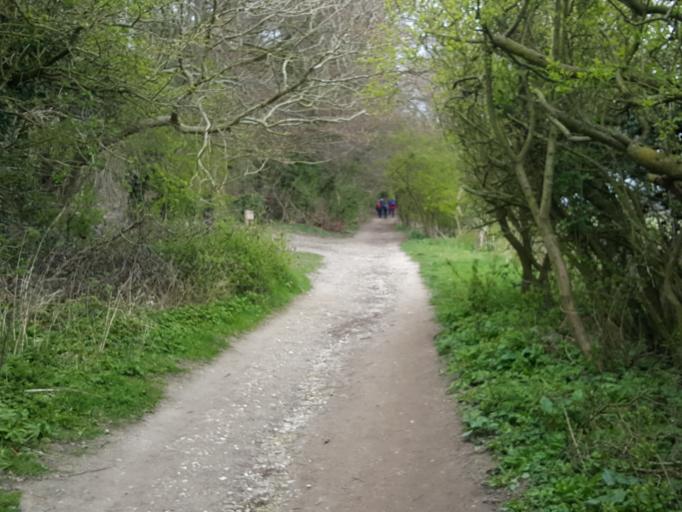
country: GB
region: England
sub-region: East Riding of Yorkshire
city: South Cave
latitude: 53.7766
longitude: -0.5915
